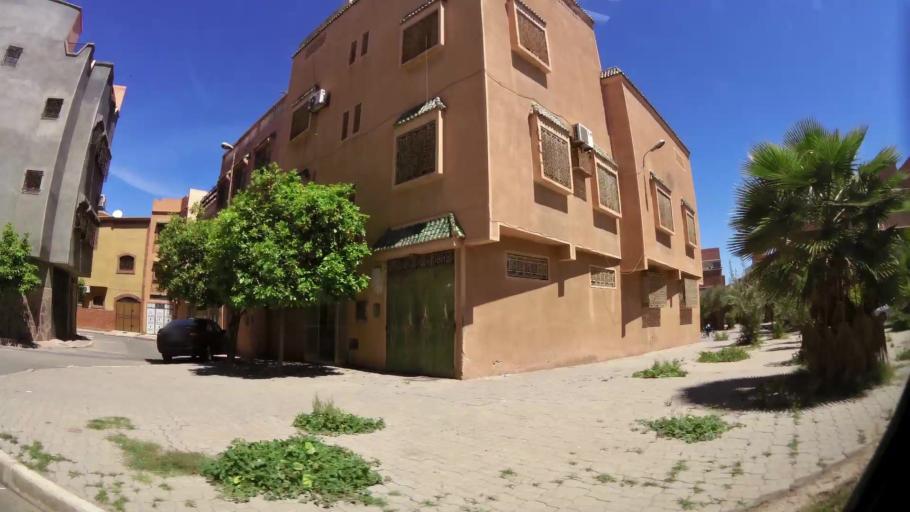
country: MA
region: Marrakech-Tensift-Al Haouz
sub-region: Marrakech
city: Marrakesh
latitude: 31.6469
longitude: -7.9993
